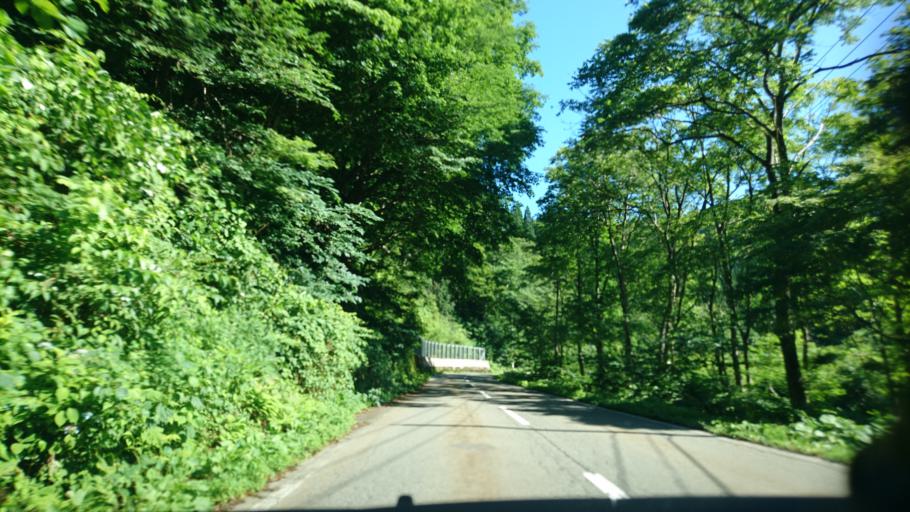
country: JP
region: Akita
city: Kakunodatemachi
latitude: 39.7134
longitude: 140.6182
